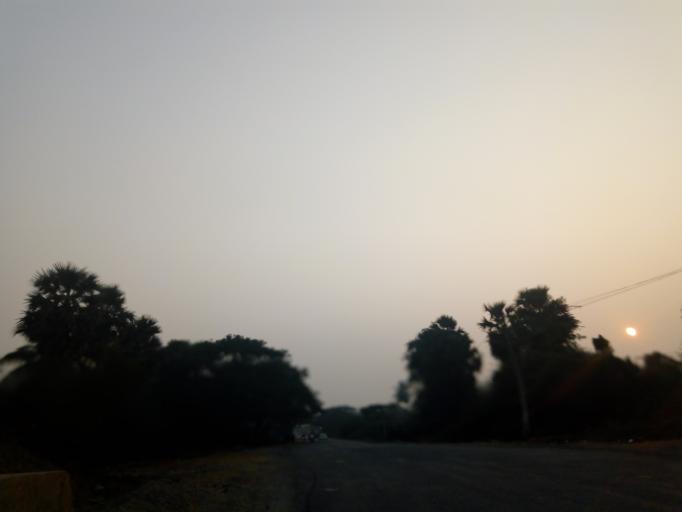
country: IN
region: Andhra Pradesh
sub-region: West Godavari
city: Tadepallegudem
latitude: 16.8590
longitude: 81.2953
